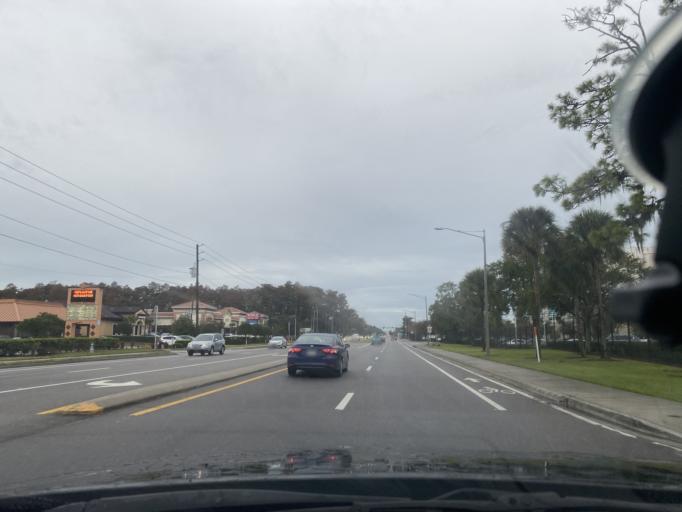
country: US
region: Florida
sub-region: Orange County
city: Azalea Park
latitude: 28.5393
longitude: -81.2789
